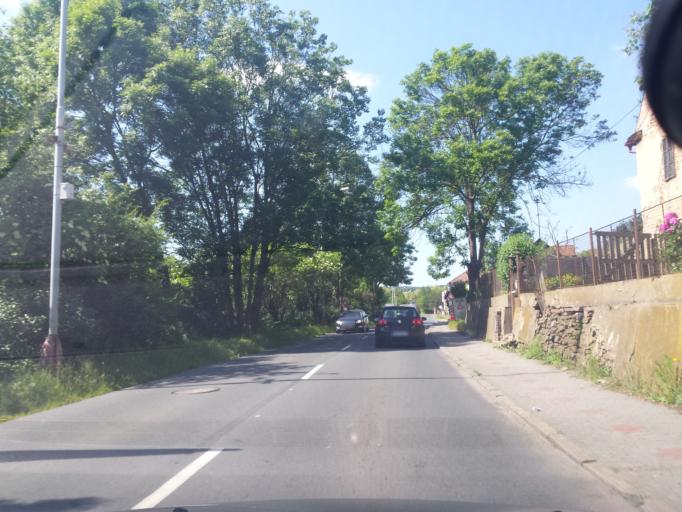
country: CZ
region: Central Bohemia
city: Kralupy nad Vltavou
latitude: 50.2264
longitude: 14.2976
